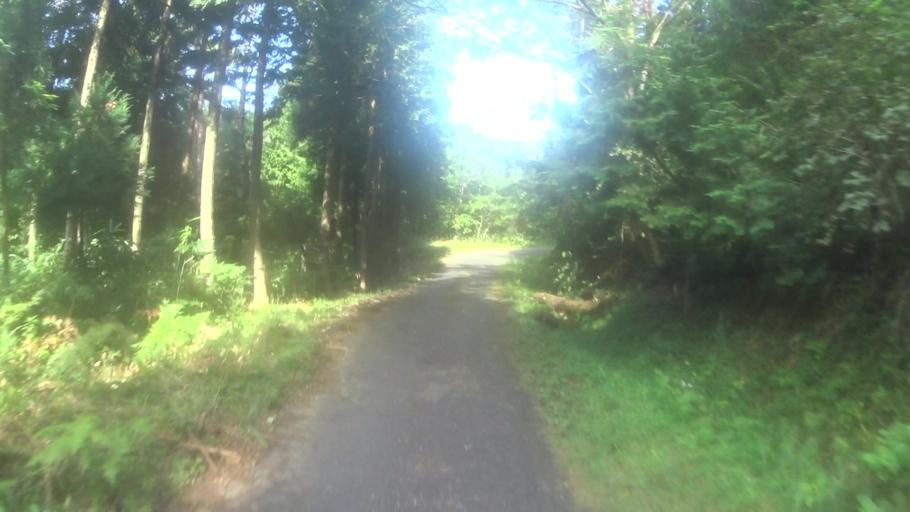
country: JP
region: Kyoto
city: Miyazu
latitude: 35.6231
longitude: 135.1577
